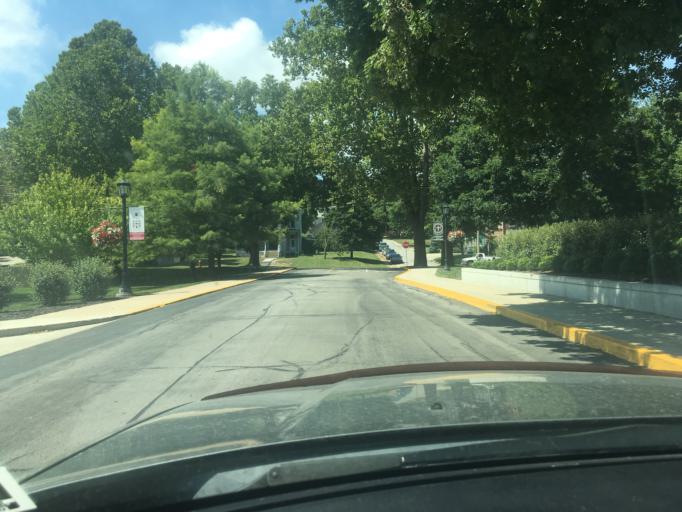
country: US
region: Kansas
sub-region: Atchison County
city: Atchison
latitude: 39.5735
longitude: -95.1143
